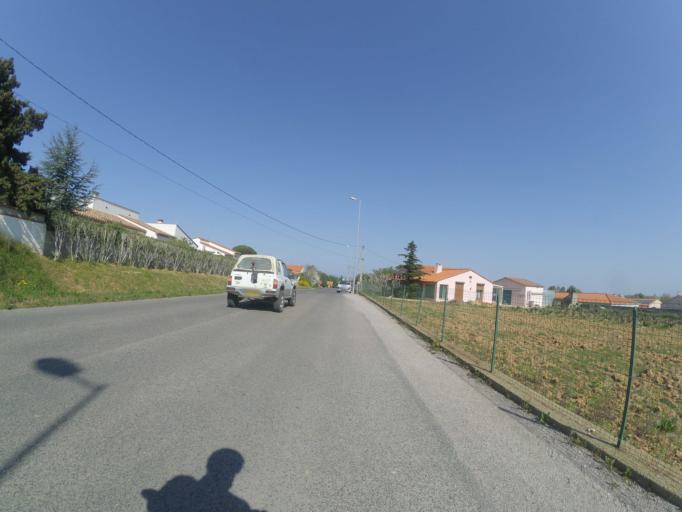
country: FR
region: Languedoc-Roussillon
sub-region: Departement des Pyrenees-Orientales
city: Llupia
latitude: 42.6260
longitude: 2.7625
